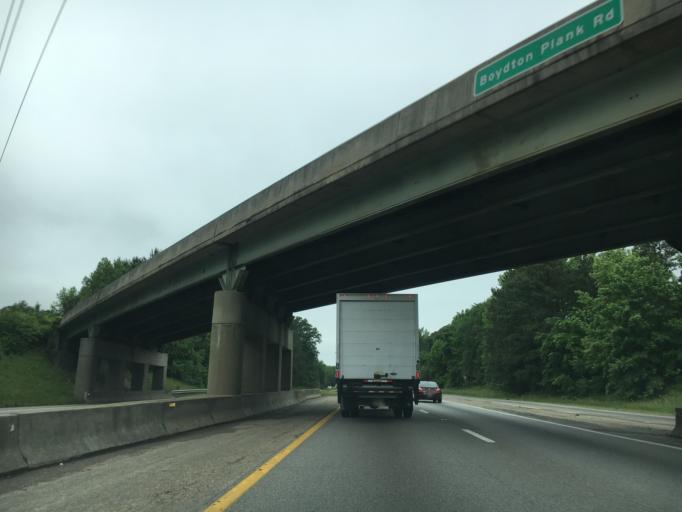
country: US
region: Virginia
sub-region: City of Petersburg
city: Petersburg
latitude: 37.2003
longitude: -77.4299
